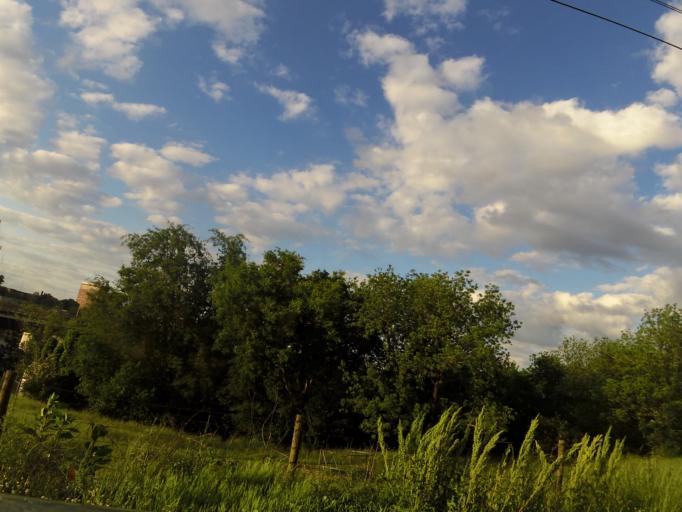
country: US
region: Tennessee
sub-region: Knox County
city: Knoxville
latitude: 35.9452
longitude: -83.9467
